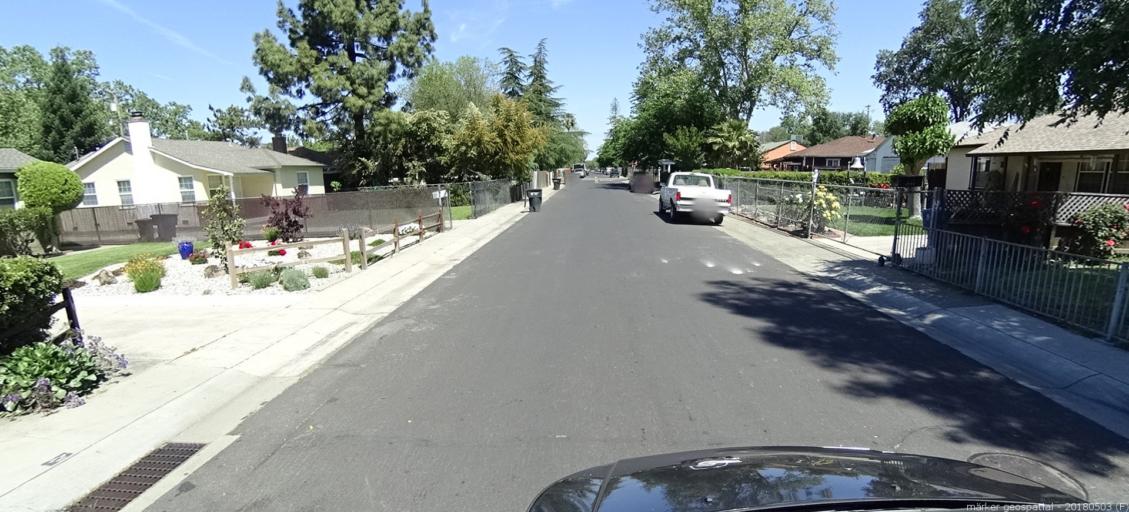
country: US
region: California
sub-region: Sacramento County
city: Arden-Arcade
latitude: 38.6355
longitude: -121.4256
